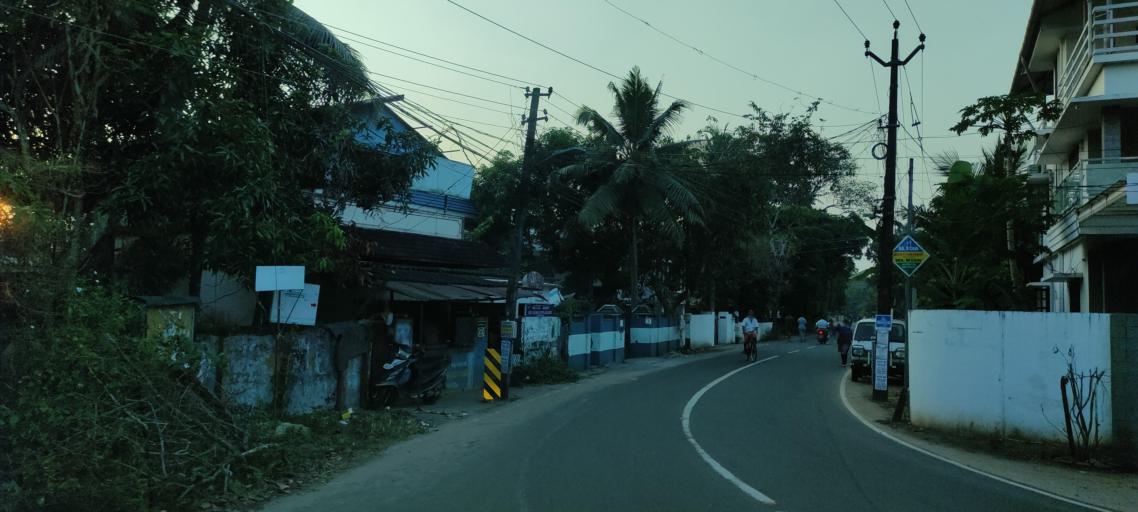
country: IN
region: Kerala
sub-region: Alappuzha
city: Alleppey
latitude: 9.4664
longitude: 76.3425
